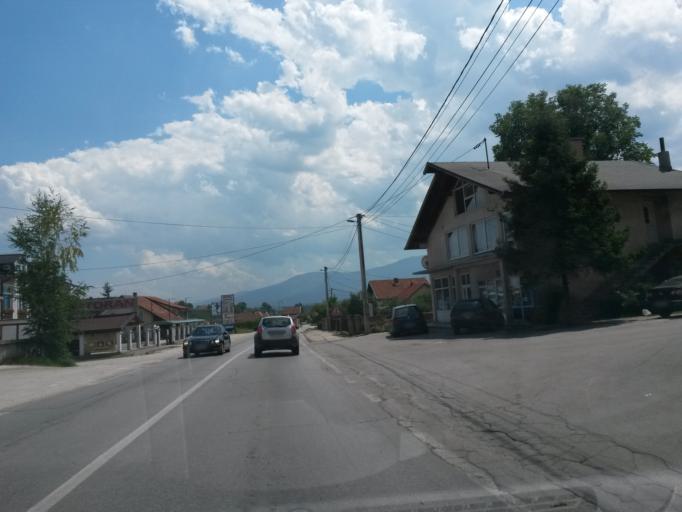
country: BA
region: Federation of Bosnia and Herzegovina
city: Vitez
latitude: 44.1791
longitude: 17.7540
